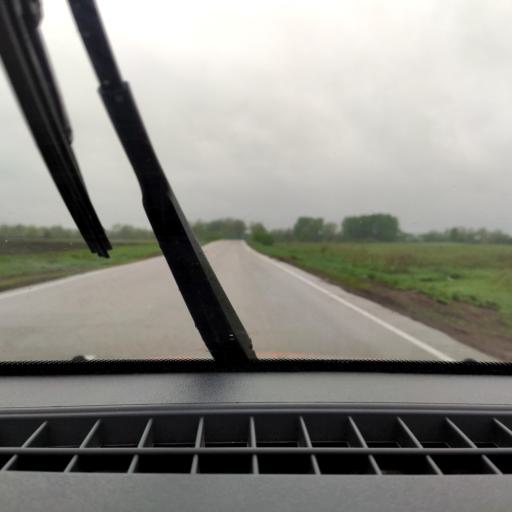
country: RU
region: Bashkortostan
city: Avdon
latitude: 54.5778
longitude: 55.8677
